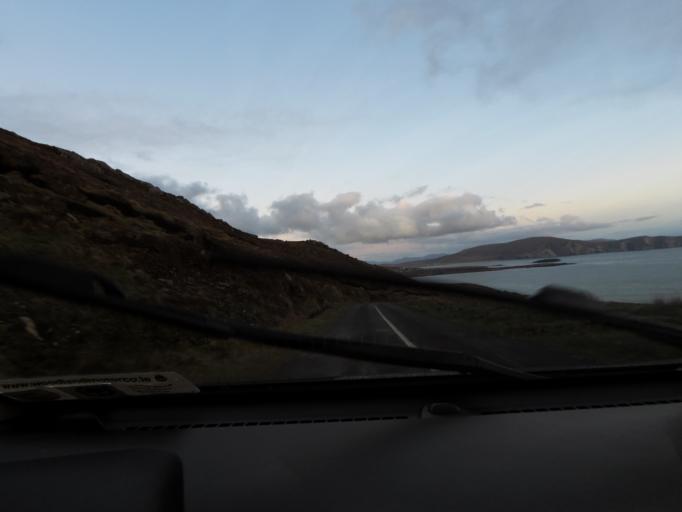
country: IE
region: Connaught
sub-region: Maigh Eo
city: Belmullet
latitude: 53.9700
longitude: -10.1654
